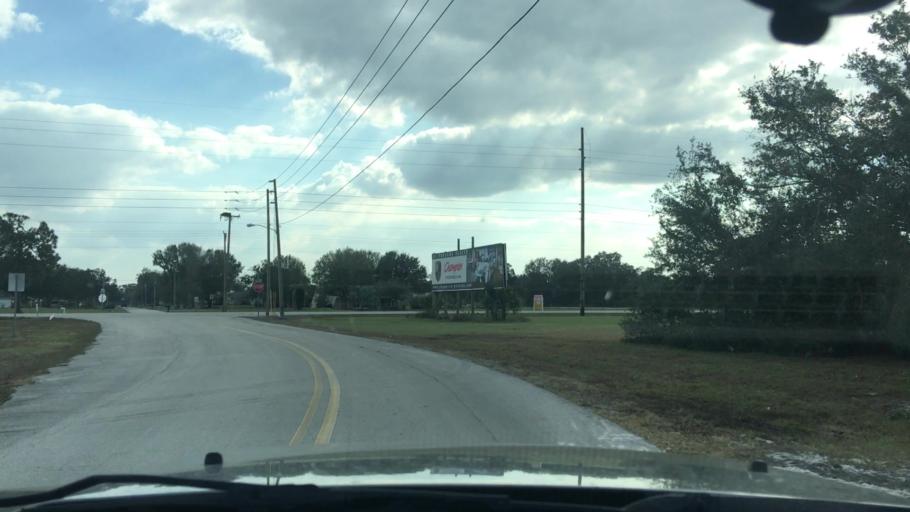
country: US
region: Florida
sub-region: Highlands County
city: Sebring
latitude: 27.4352
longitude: -81.3631
